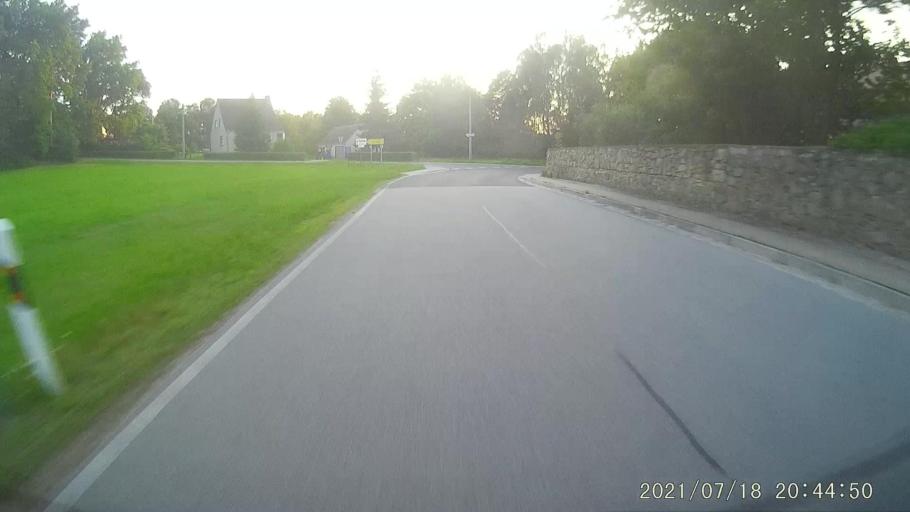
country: DE
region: Saxony
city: Reichenbach
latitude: 51.1959
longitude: 14.7779
